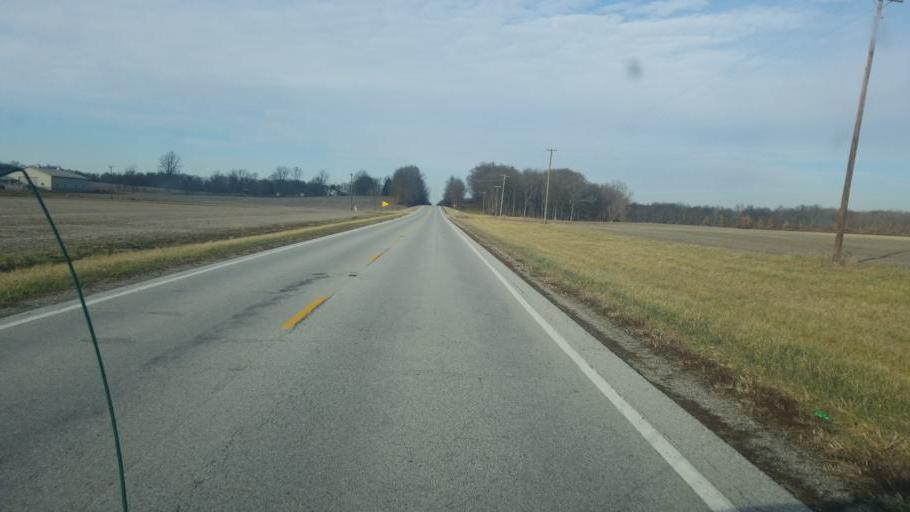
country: US
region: Illinois
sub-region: Wabash County
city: Mount Carmel
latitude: 38.5557
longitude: -87.6949
